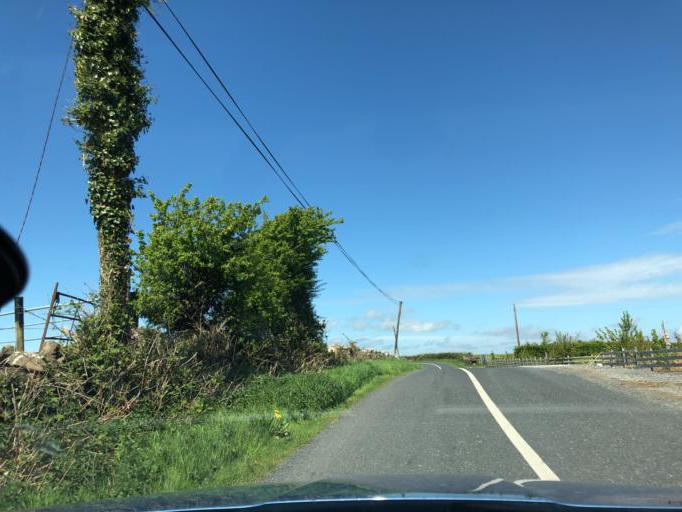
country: IE
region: Connaught
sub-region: County Galway
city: Loughrea
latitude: 53.1654
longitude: -8.4091
